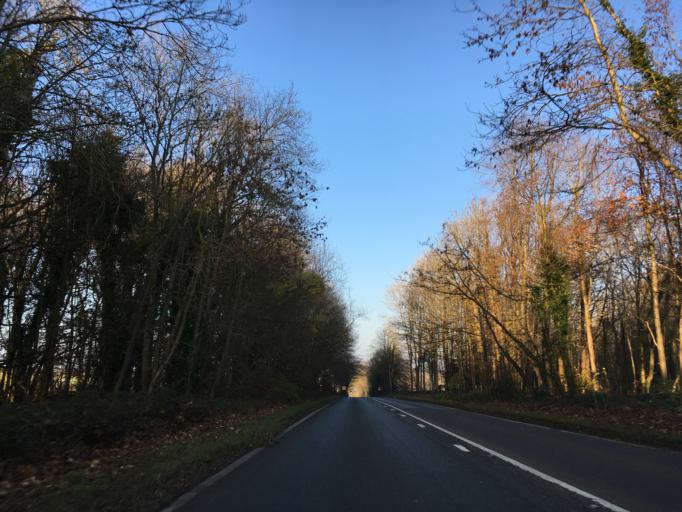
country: GB
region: England
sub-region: South Gloucestershire
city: Horton
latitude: 51.5630
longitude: -2.3113
